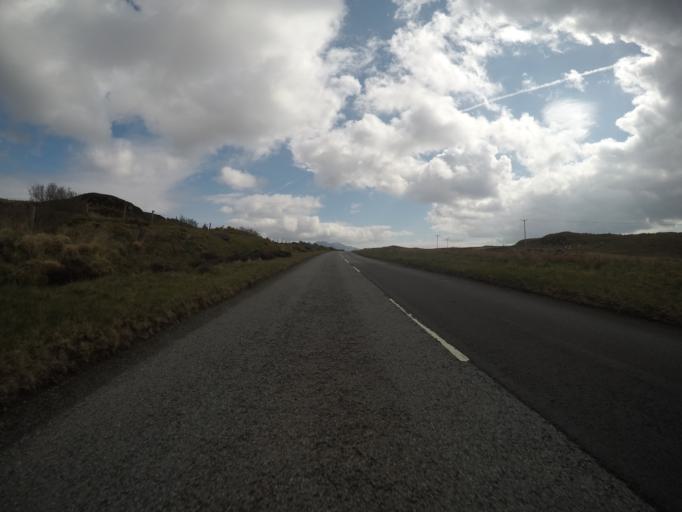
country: GB
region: Scotland
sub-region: Highland
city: Isle of Skye
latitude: 57.3181
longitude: -6.3222
